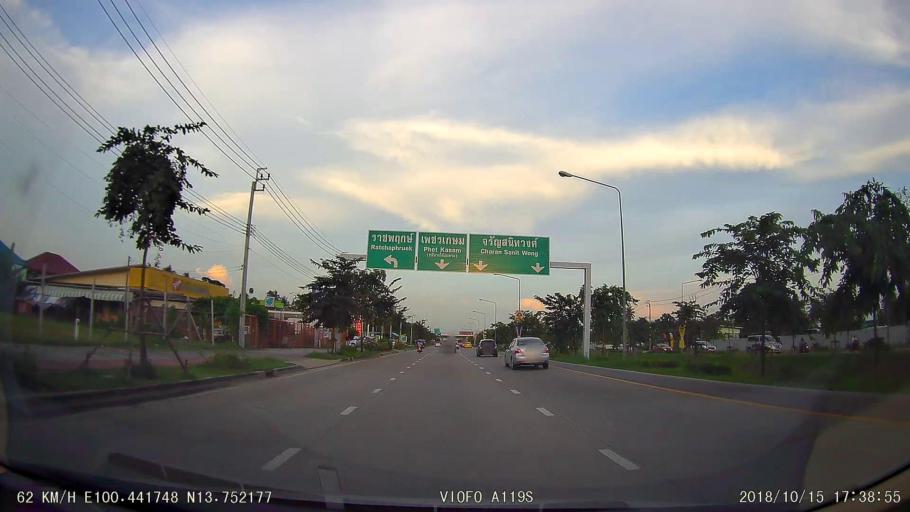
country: TH
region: Bangkok
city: Taling Chan
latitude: 13.7522
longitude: 100.4420
